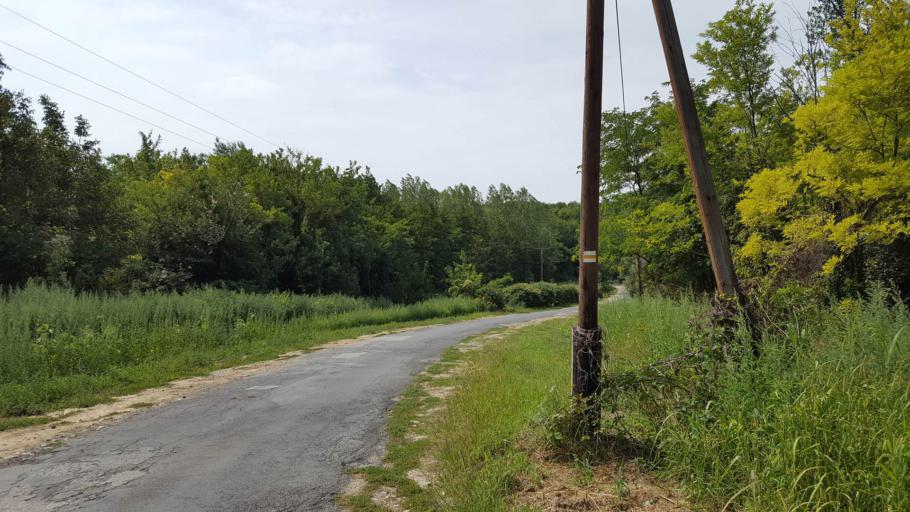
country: HU
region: Somogy
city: Somogyvar
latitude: 46.5811
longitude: 17.6772
